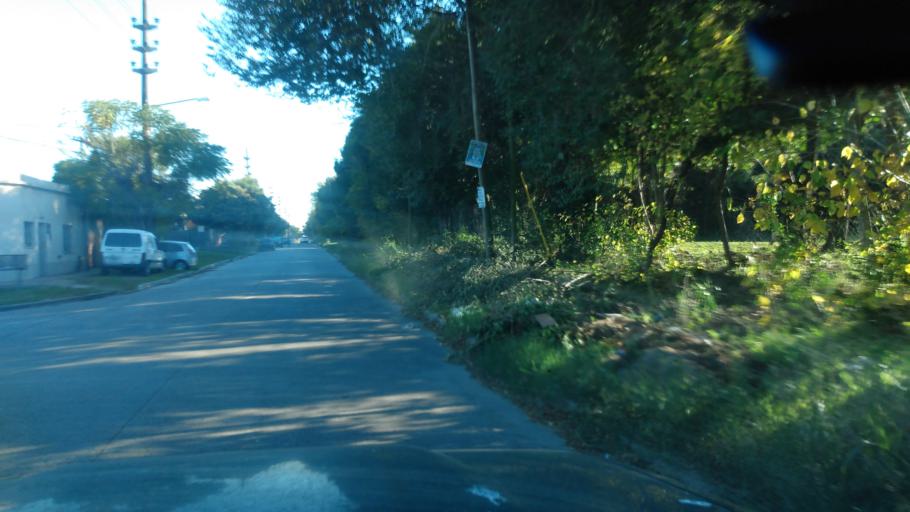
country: AR
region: Buenos Aires
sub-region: Partido de Lujan
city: Lujan
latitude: -34.5598
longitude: -59.1012
